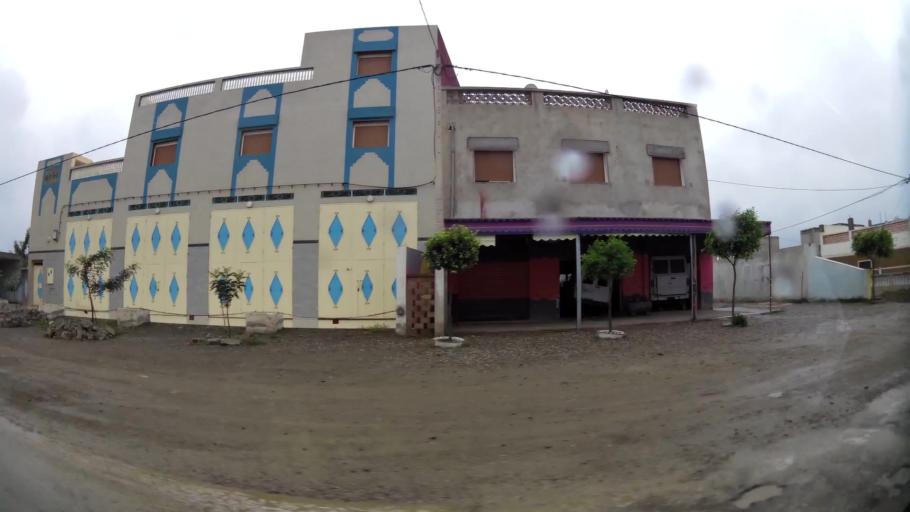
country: MA
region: Taza-Al Hoceima-Taounate
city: Imzourene
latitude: 35.1540
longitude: -3.8282
